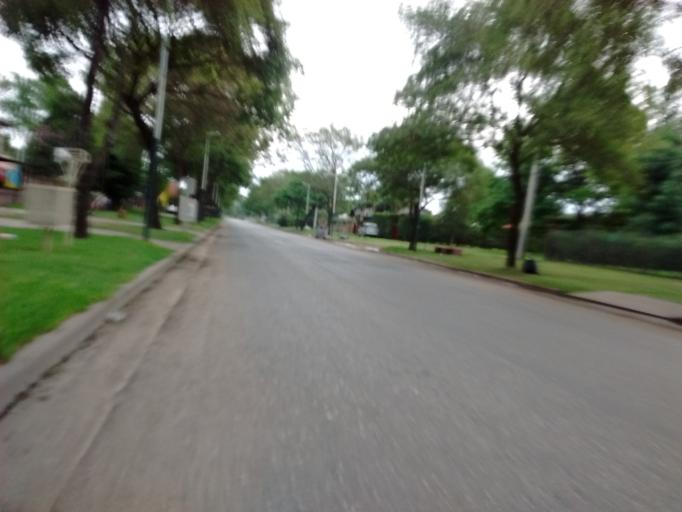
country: AR
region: Santa Fe
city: Funes
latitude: -32.9263
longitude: -60.8118
